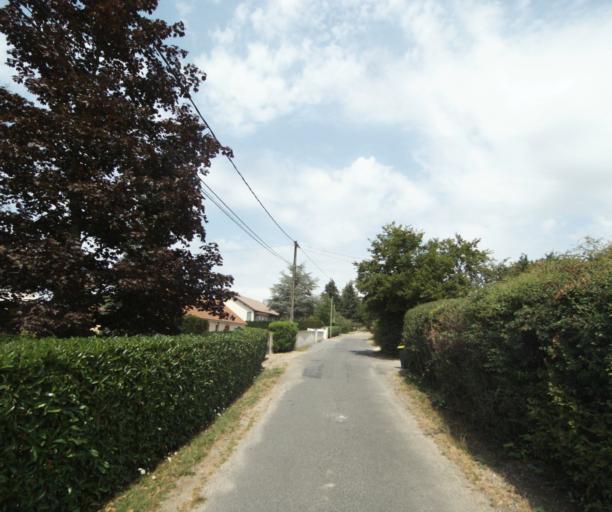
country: FR
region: Bourgogne
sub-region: Departement de Saone-et-Loire
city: Gueugnon
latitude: 46.6045
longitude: 4.0135
